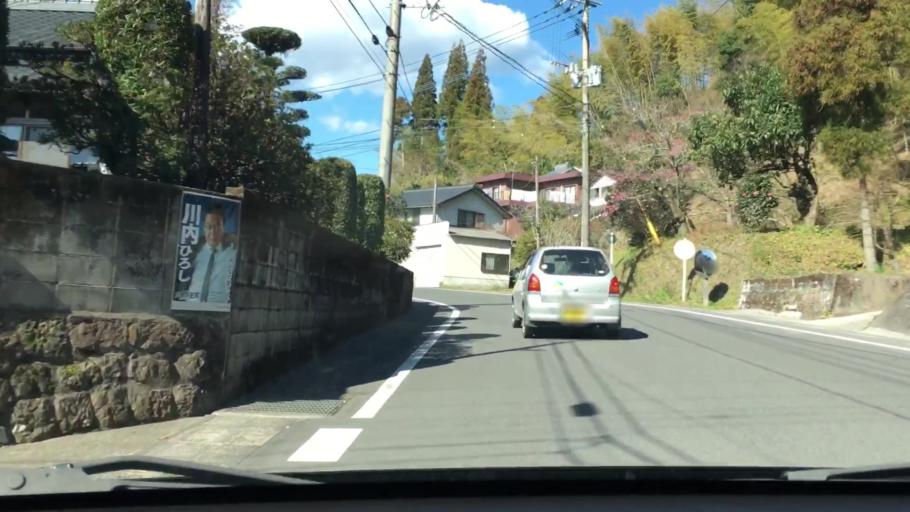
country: JP
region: Kagoshima
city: Ijuin
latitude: 31.6885
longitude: 130.4675
